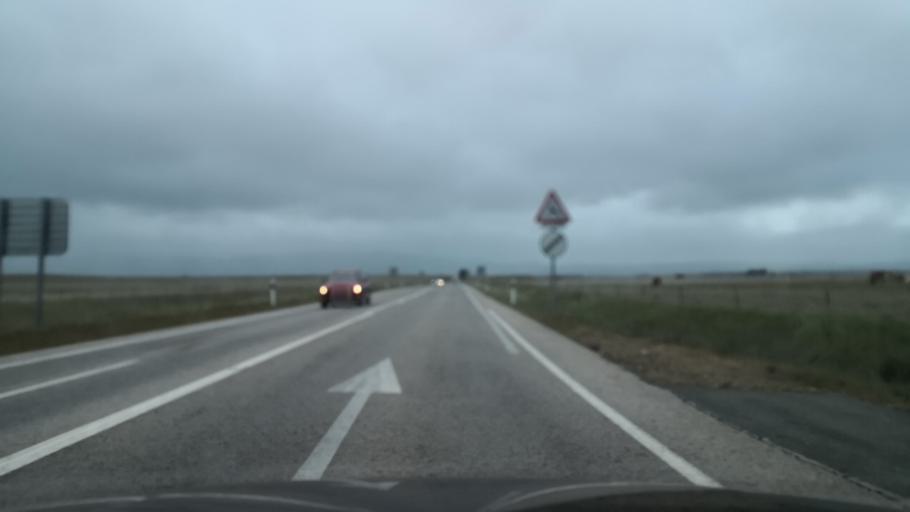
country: ES
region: Extremadura
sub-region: Provincia de Caceres
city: Malpartida de Caceres
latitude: 39.3604
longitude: -6.4636
